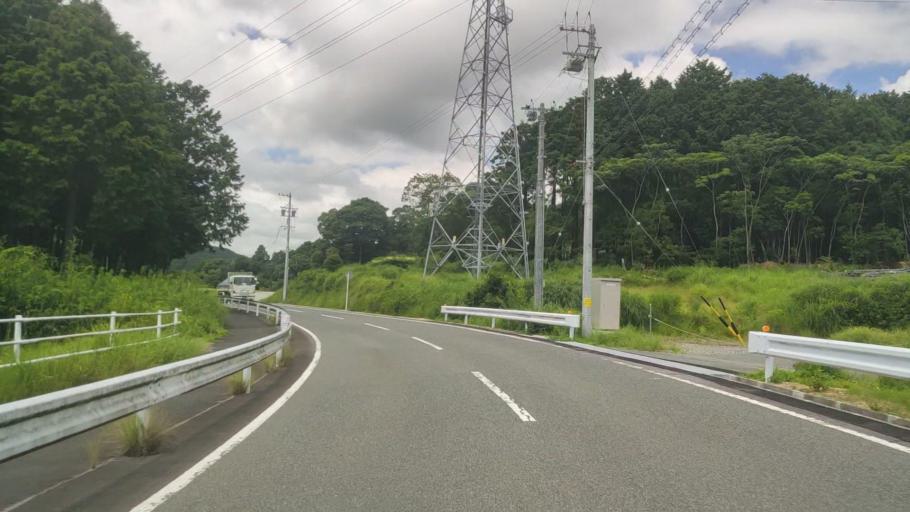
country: JP
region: Mie
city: Toba
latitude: 34.3878
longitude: 136.8055
